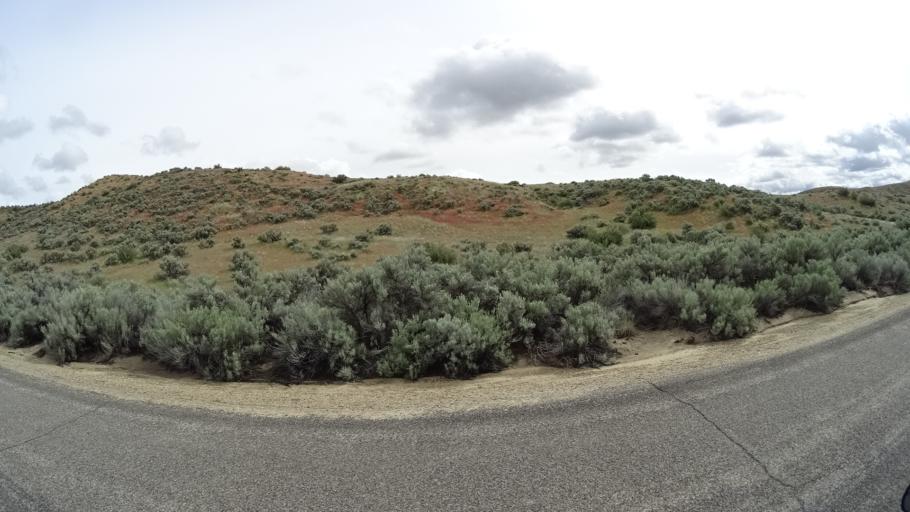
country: US
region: Idaho
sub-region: Ada County
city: Eagle
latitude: 43.7498
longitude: -116.3586
